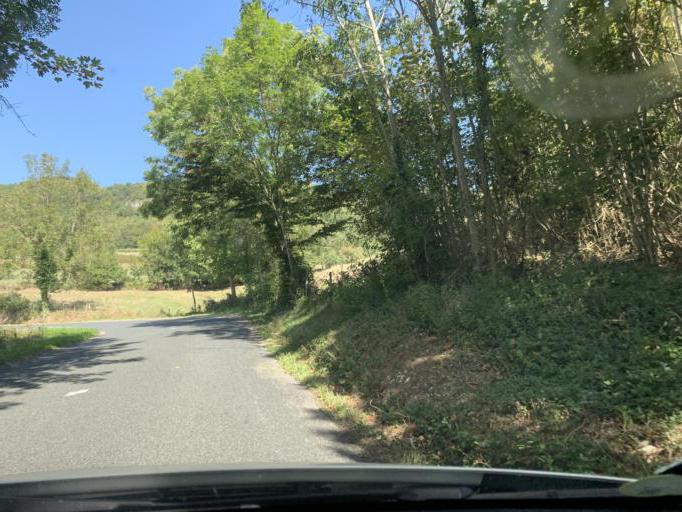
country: FR
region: Rhone-Alpes
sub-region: Departement de la Savoie
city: Saint-Genix-sur-Guiers
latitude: 45.6479
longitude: 5.6351
